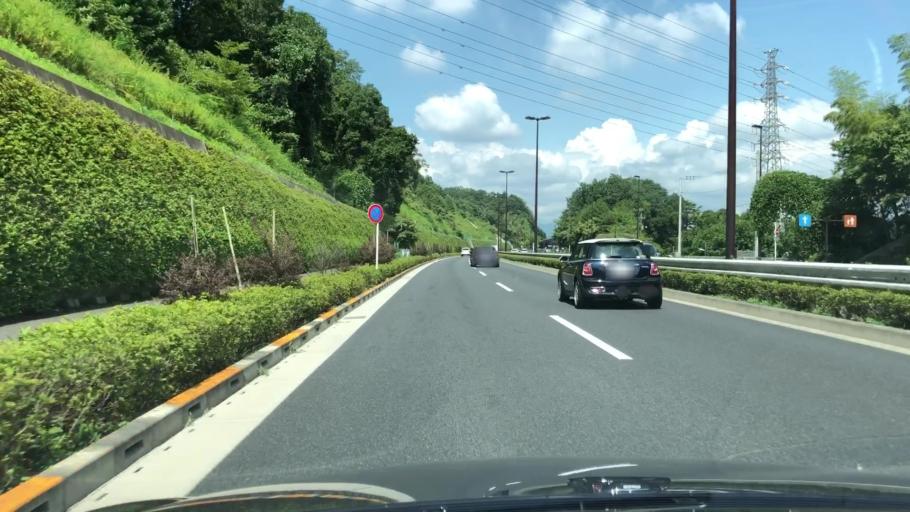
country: JP
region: Tokyo
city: Fussa
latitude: 35.6988
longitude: 139.3152
